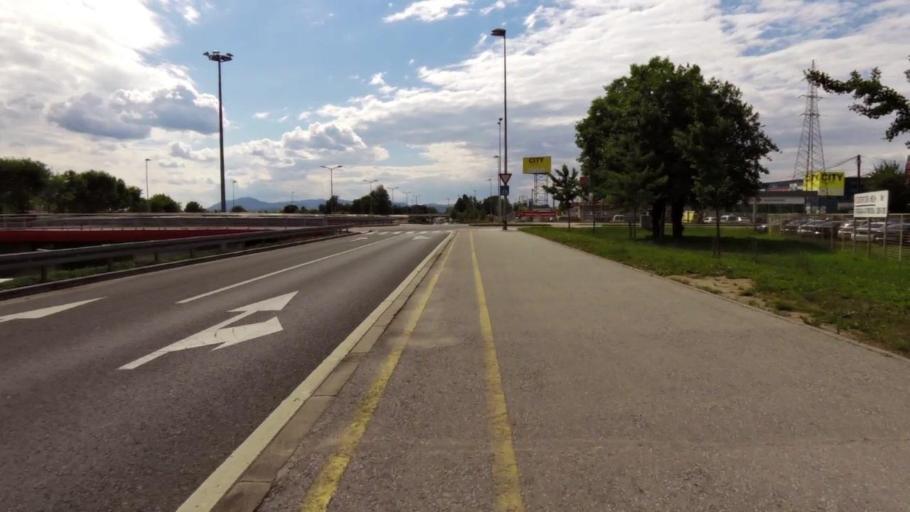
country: HR
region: Grad Zagreb
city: Stenjevec
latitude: 45.7974
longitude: 15.8883
